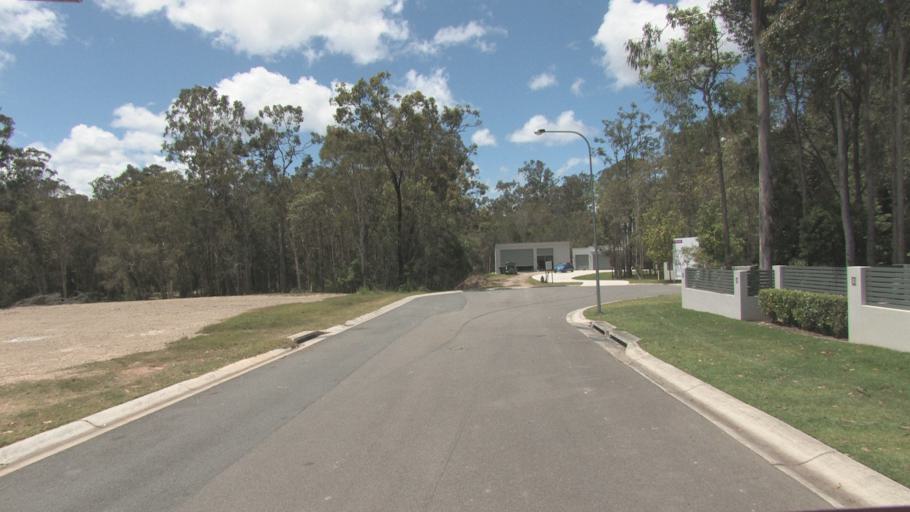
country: AU
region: Queensland
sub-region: Logan
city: Beenleigh
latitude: -27.6644
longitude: 153.2198
